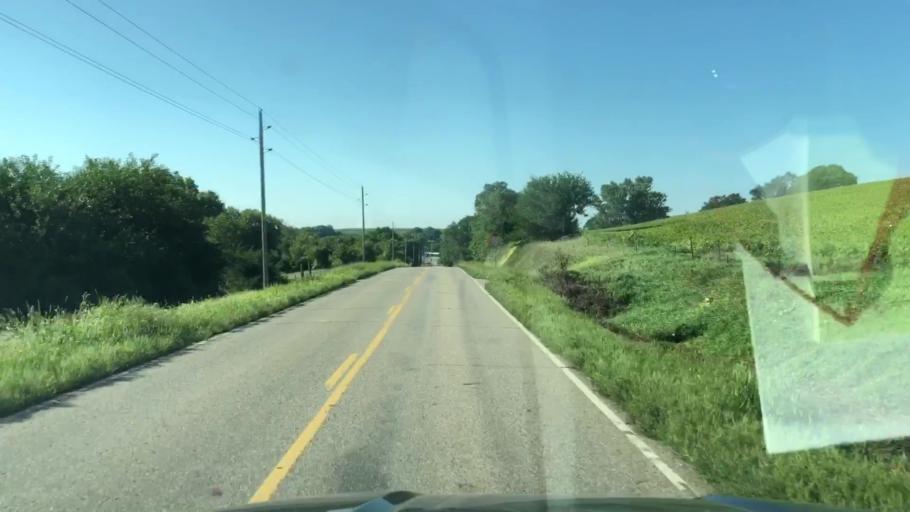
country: US
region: Iowa
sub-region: Woodbury County
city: Sergeant Bluff
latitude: 42.4147
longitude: -96.2138
